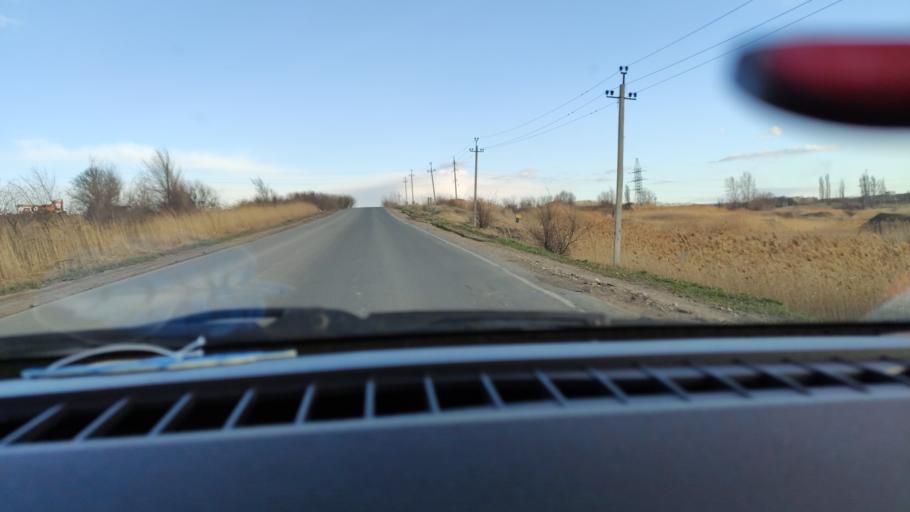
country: RU
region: Saratov
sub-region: Saratovskiy Rayon
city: Saratov
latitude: 51.6157
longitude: 45.9497
